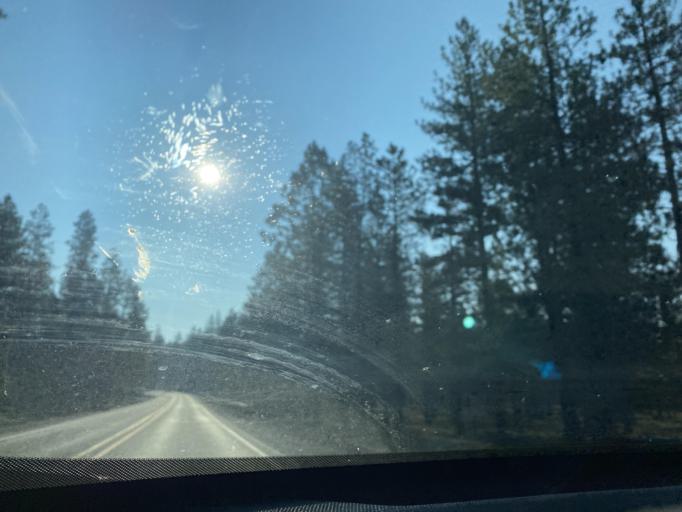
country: US
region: Oregon
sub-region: Deschutes County
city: Sunriver
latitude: 43.8694
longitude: -121.4169
